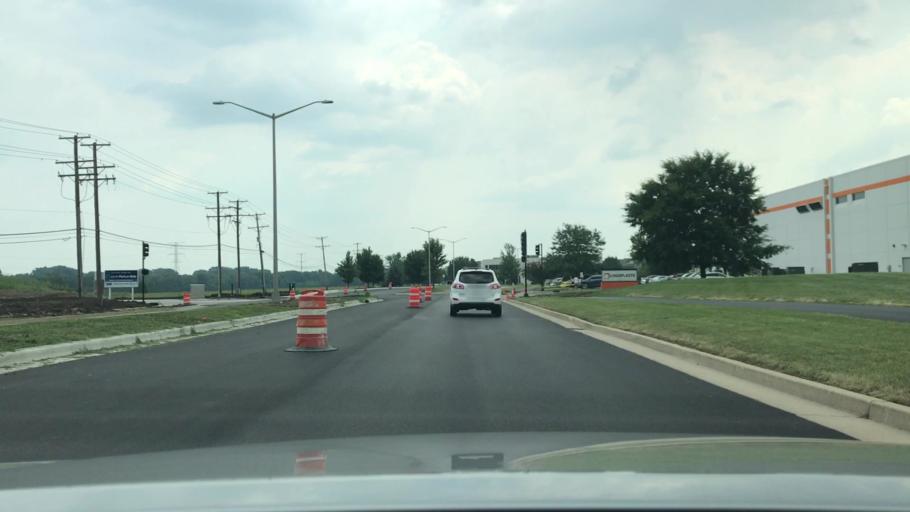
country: US
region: Illinois
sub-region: Will County
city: Plainfield
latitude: 41.6205
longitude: -88.2123
